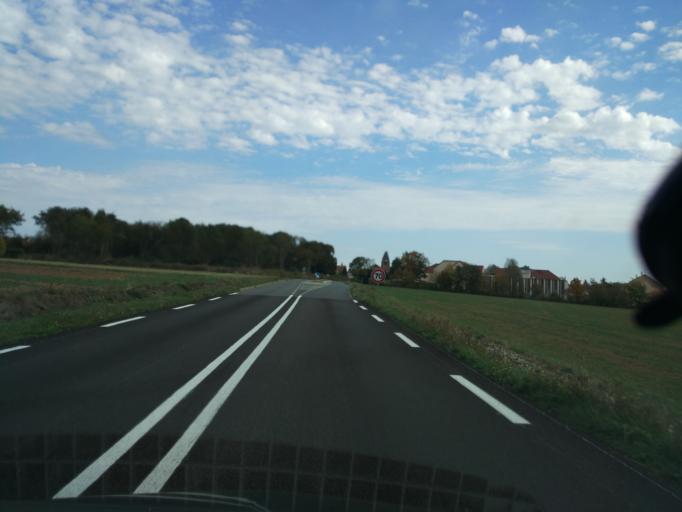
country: FR
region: Ile-de-France
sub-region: Departement de l'Essonne
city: Gometz-la-Ville
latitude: 48.6725
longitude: 2.1182
